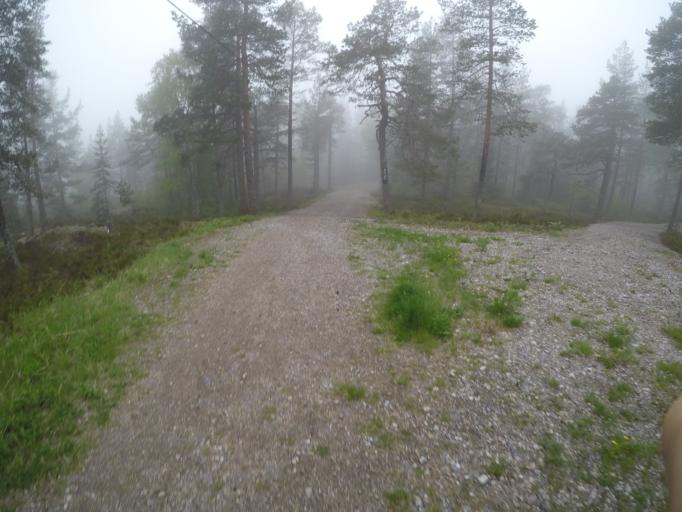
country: SE
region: Vaesternorrland
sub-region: Sundsvalls Kommun
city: Sundsvall
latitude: 62.3660
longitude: 17.3109
